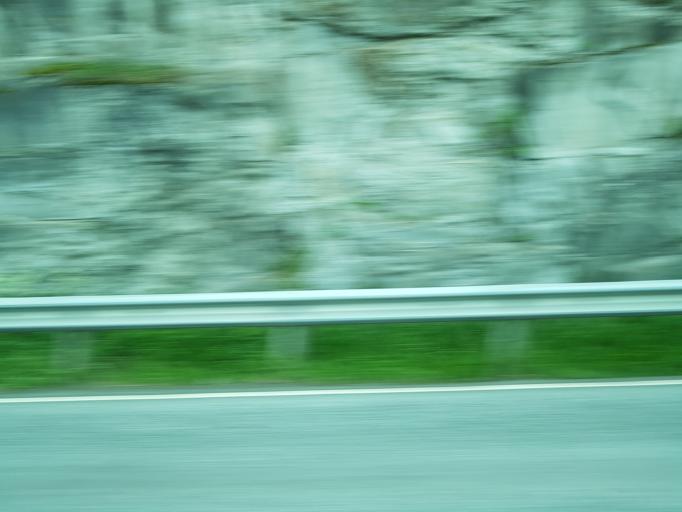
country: NO
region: Nord-Trondelag
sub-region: Stjordal
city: Stjordal
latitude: 63.5441
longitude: 10.8731
